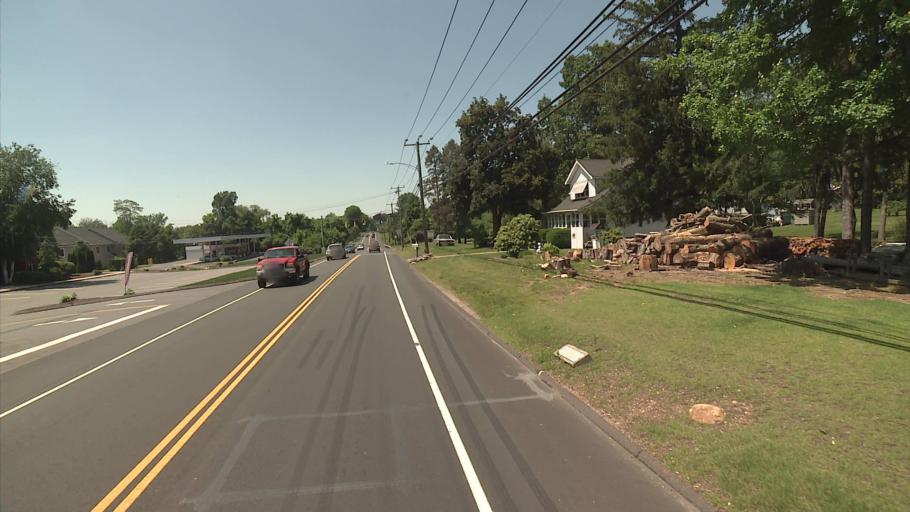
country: US
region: Connecticut
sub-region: Hartford County
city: Manchester
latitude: 41.8212
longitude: -72.5428
